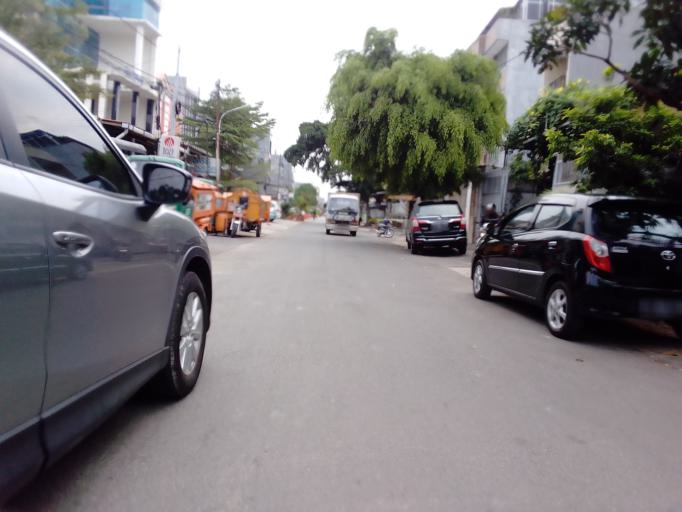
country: ID
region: Jakarta Raya
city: Jakarta
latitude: -6.1553
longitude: 106.8167
